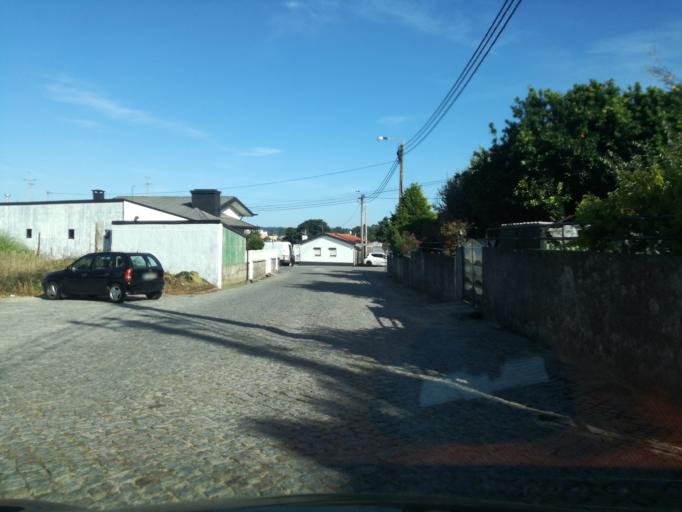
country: PT
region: Porto
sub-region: Maia
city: Nogueira
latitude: 41.2629
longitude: -8.5984
